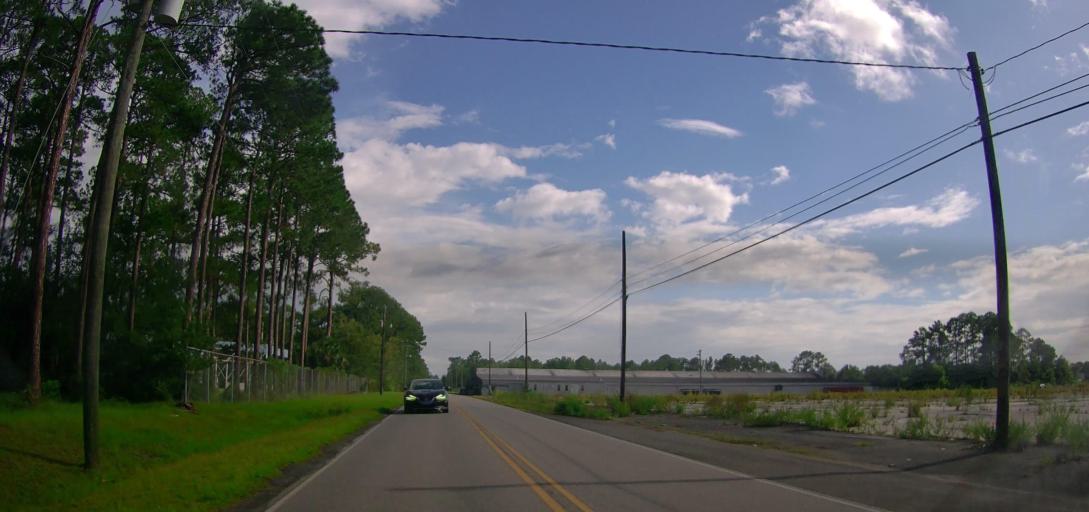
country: US
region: Georgia
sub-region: Coffee County
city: Douglas
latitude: 31.4939
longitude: -82.8589
